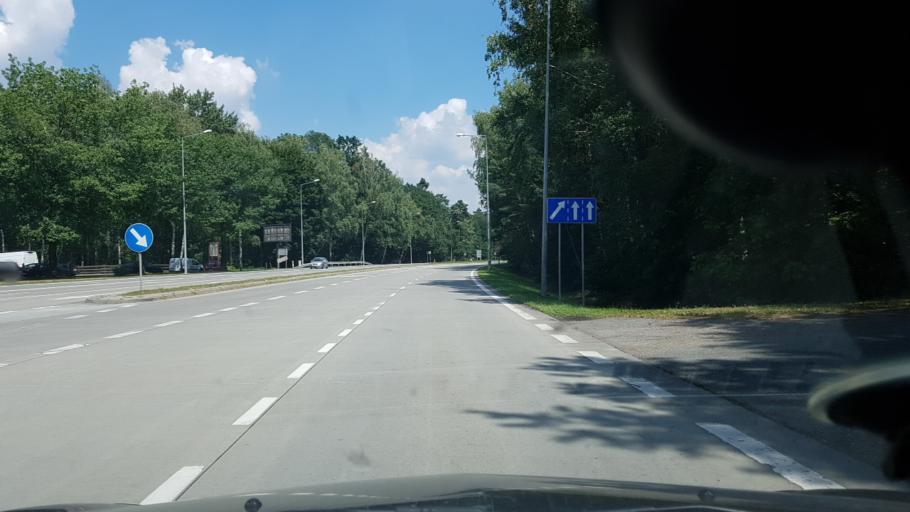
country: PL
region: Silesian Voivodeship
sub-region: Zory
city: Zory
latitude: 50.0620
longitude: 18.7238
